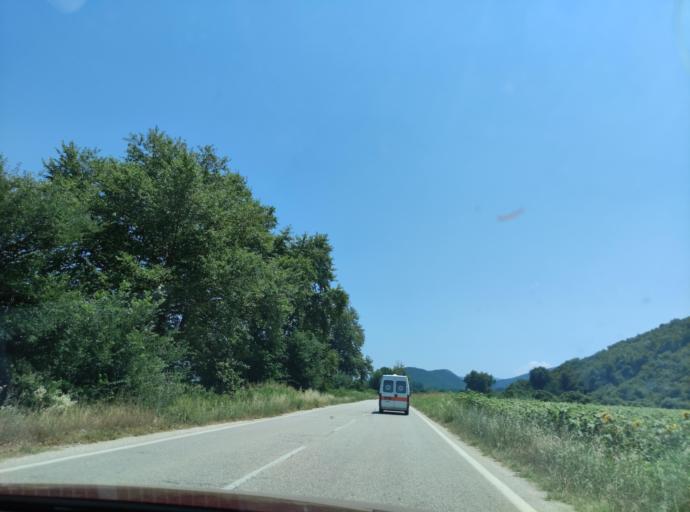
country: GR
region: East Macedonia and Thrace
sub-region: Nomos Kavalas
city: Palaiochori
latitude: 40.9681
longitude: 24.1760
